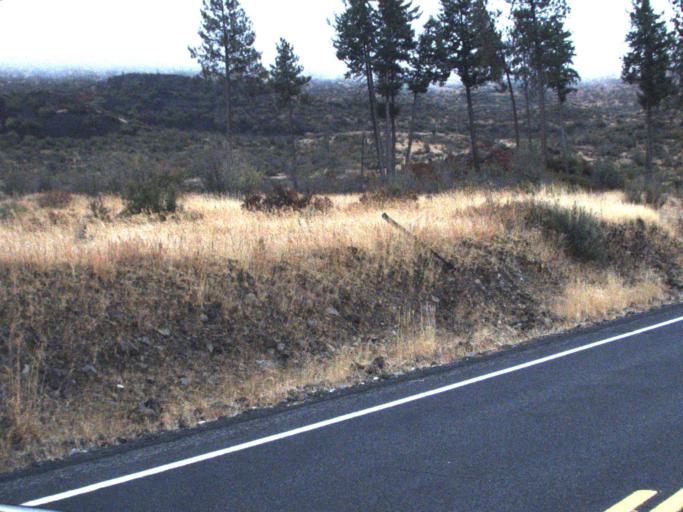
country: US
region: Washington
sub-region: Spokane County
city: Fairchild Air Force Base
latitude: 47.7813
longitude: -117.8886
